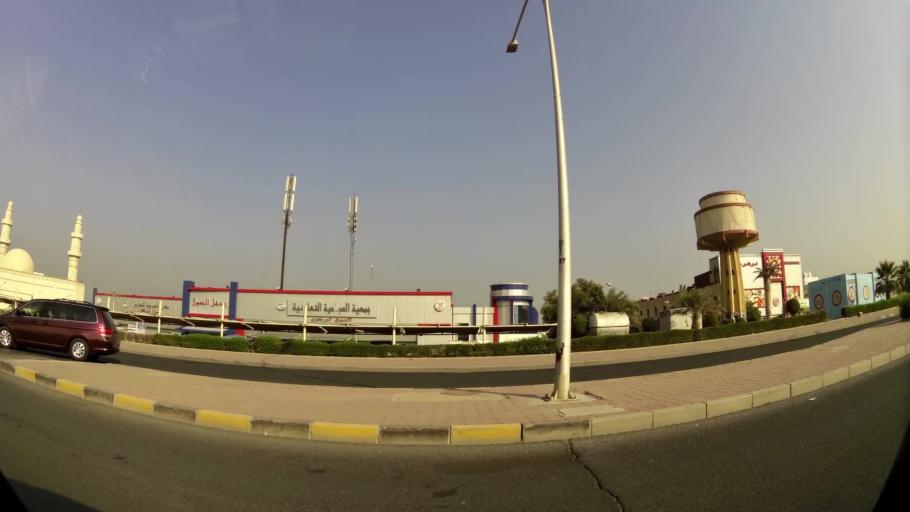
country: KW
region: Al Ahmadi
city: Al Manqaf
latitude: 29.1067
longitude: 48.1055
